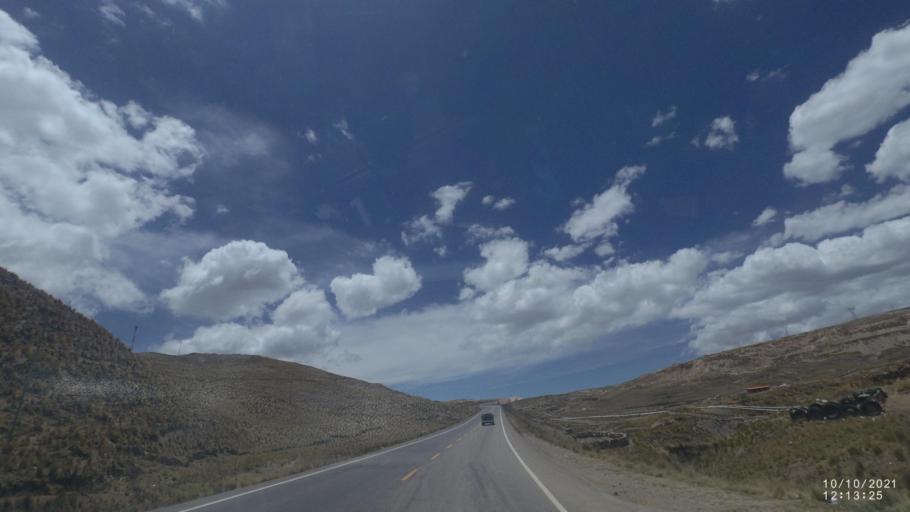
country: BO
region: Cochabamba
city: Irpa Irpa
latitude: -17.6923
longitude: -66.5143
